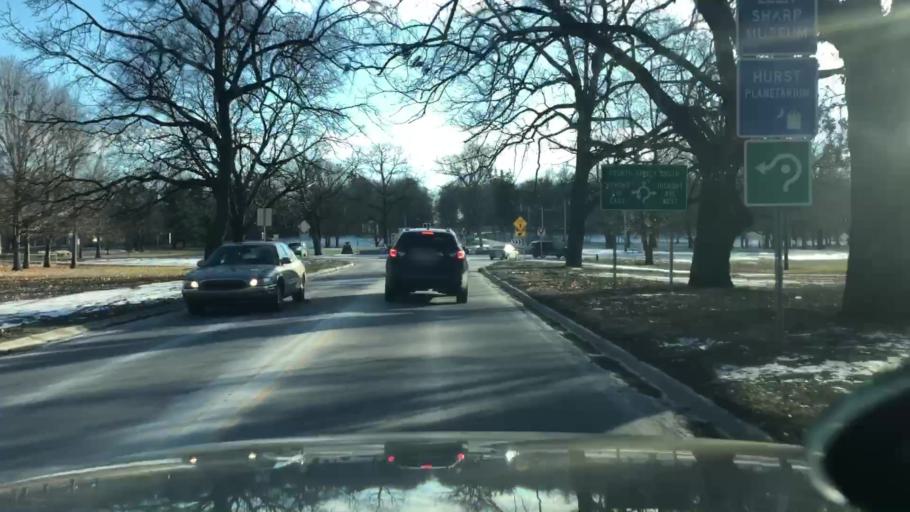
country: US
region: Michigan
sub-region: Jackson County
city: Jackson
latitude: 42.2182
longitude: -84.4183
